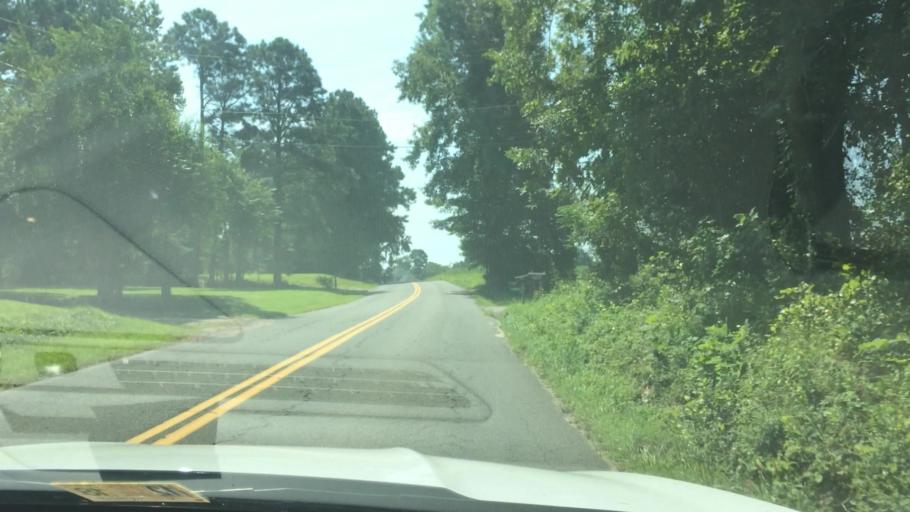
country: US
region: Virginia
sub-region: Henrico County
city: Sandston
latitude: 37.5249
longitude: -77.1674
